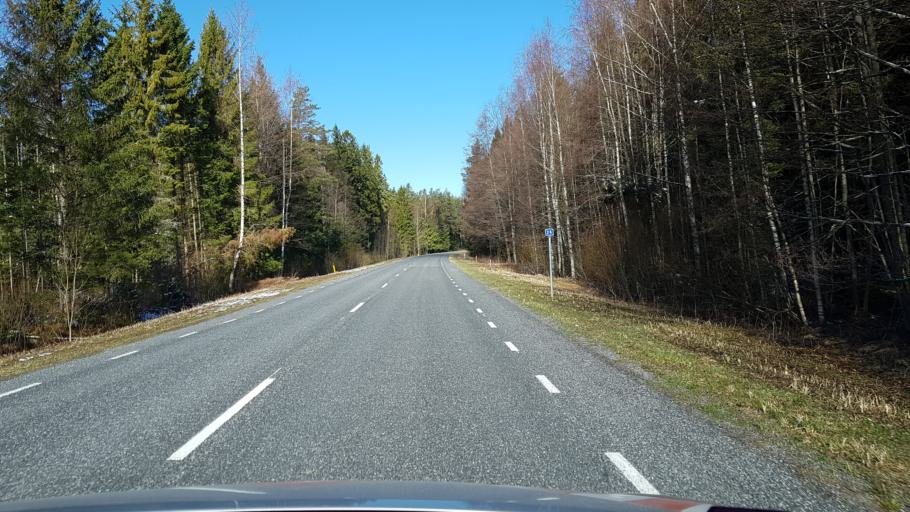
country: EE
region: Harju
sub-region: Loksa linn
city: Loksa
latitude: 59.5677
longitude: 25.9397
